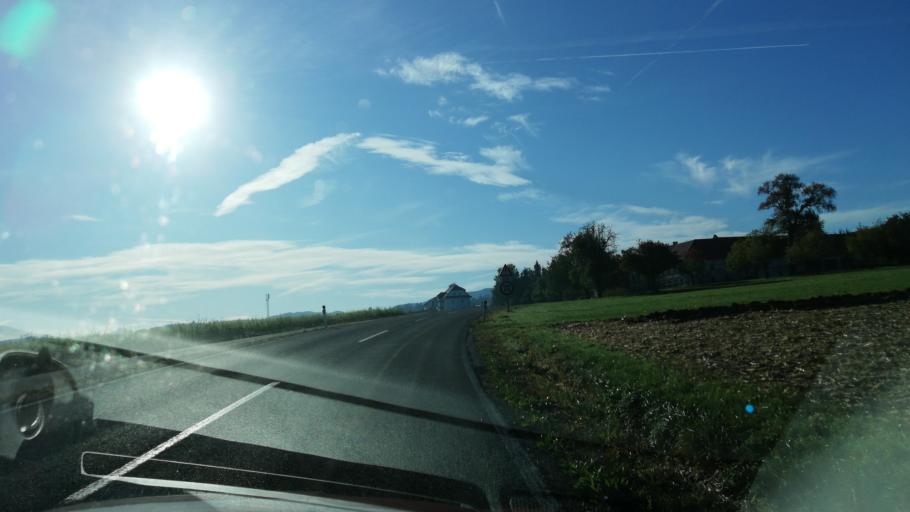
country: AT
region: Upper Austria
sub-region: Politischer Bezirk Steyr-Land
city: Waldneukirchen
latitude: 48.0111
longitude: 14.2461
